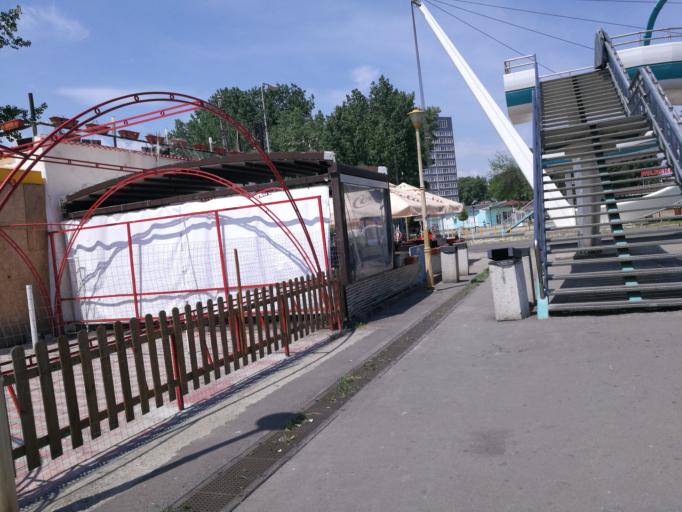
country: RO
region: Constanta
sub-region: Municipiul Constanta
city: Palazu Mare
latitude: 44.2184
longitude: 28.6317
